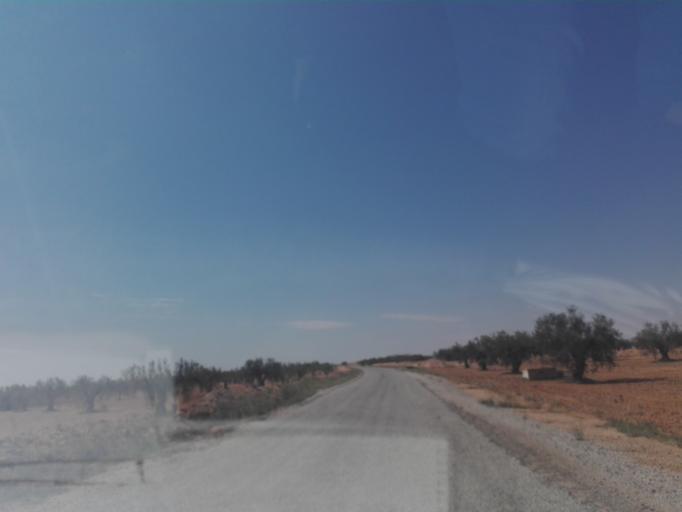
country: TN
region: Safaqis
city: Bi'r `Ali Bin Khalifah
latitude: 34.6470
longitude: 10.4111
